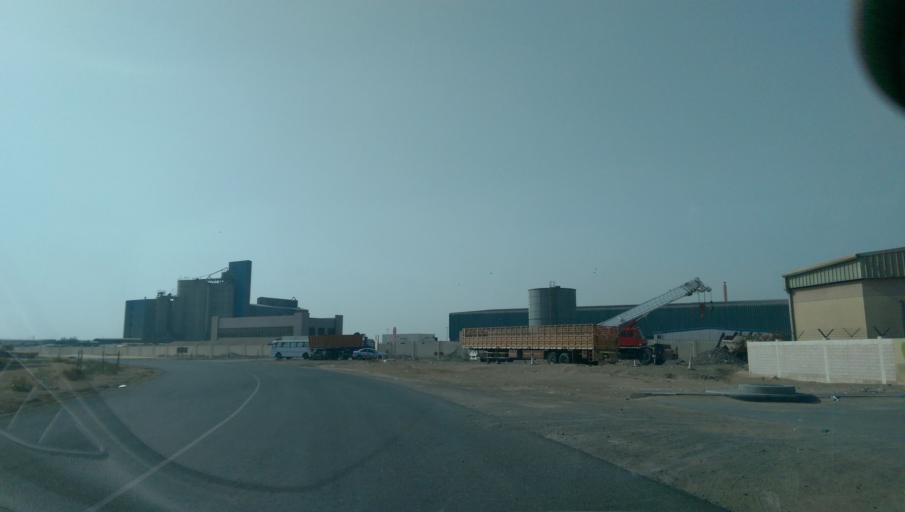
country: AE
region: Abu Dhabi
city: Abu Dhabi
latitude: 24.3251
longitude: 54.4801
